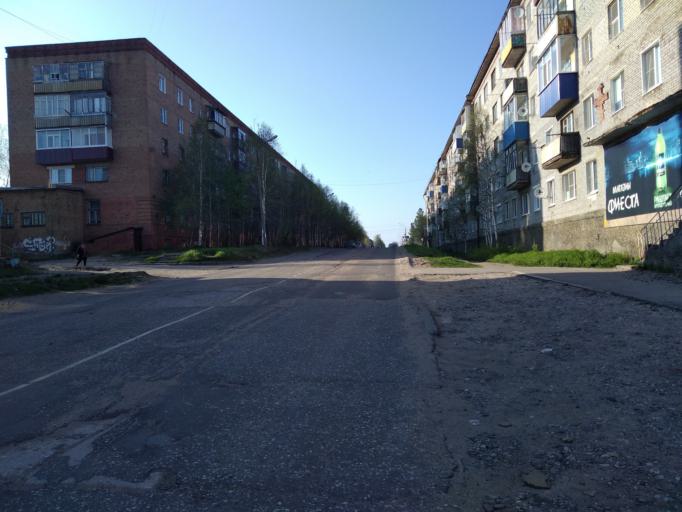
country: RU
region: Komi Republic
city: Pechora
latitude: 65.1077
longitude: 57.1542
